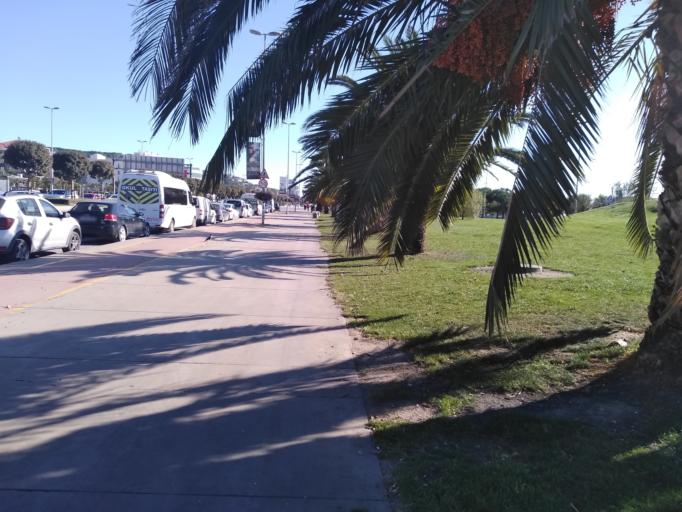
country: TR
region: Istanbul
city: Maltepe
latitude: 40.9170
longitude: 29.1307
